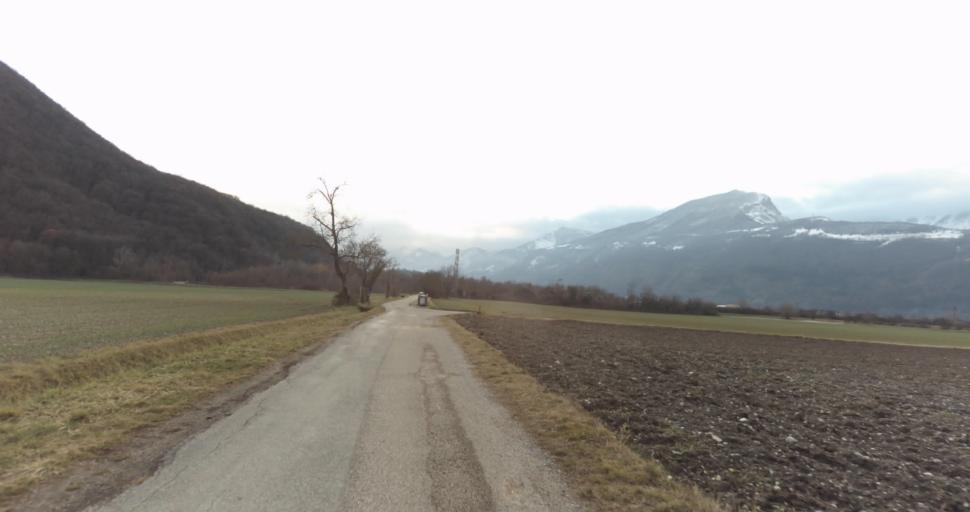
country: FR
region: Rhone-Alpes
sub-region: Departement de l'Isere
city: Vif
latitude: 45.0592
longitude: 5.6896
